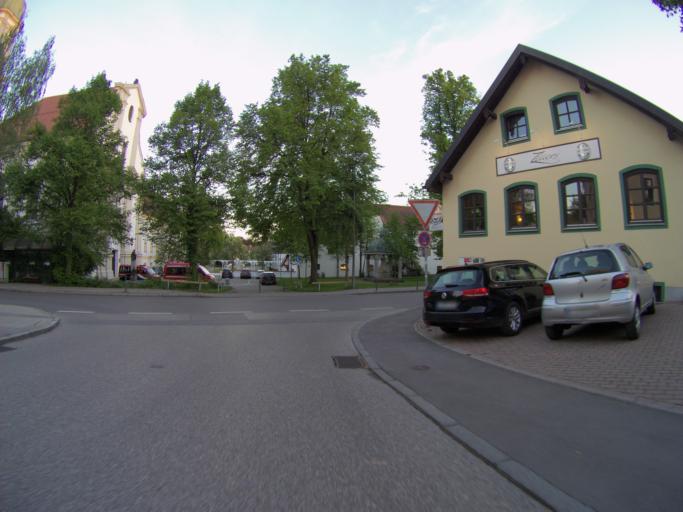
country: DE
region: Bavaria
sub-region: Upper Bavaria
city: Freising
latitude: 48.4072
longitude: 11.7576
